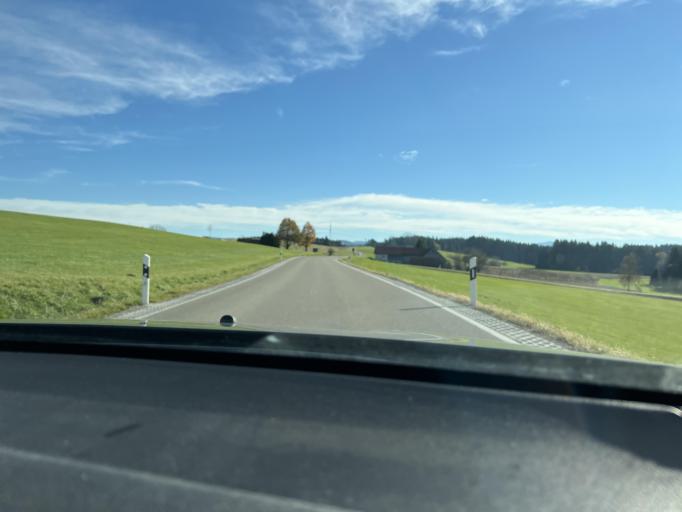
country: DE
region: Bavaria
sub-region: Swabia
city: Gestratz
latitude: 47.7113
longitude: 9.9698
